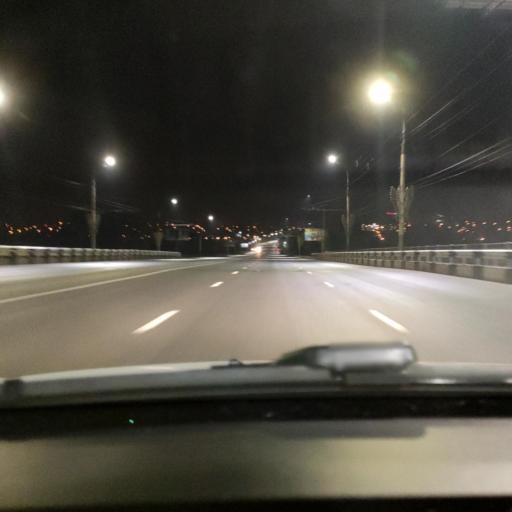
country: RU
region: Voronezj
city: Voronezh
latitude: 51.6338
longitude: 39.2212
